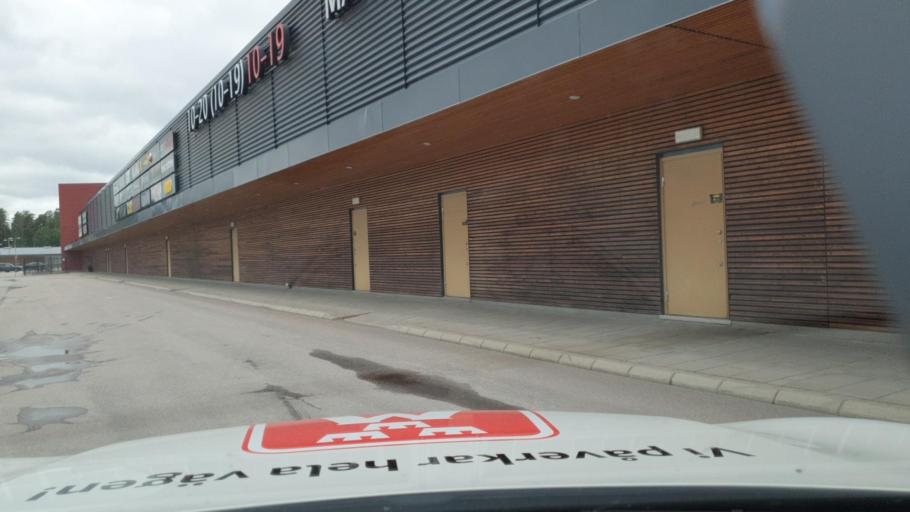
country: SE
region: Vaermland
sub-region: Eda Kommun
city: Charlottenberg
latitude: 59.8807
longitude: 12.2902
